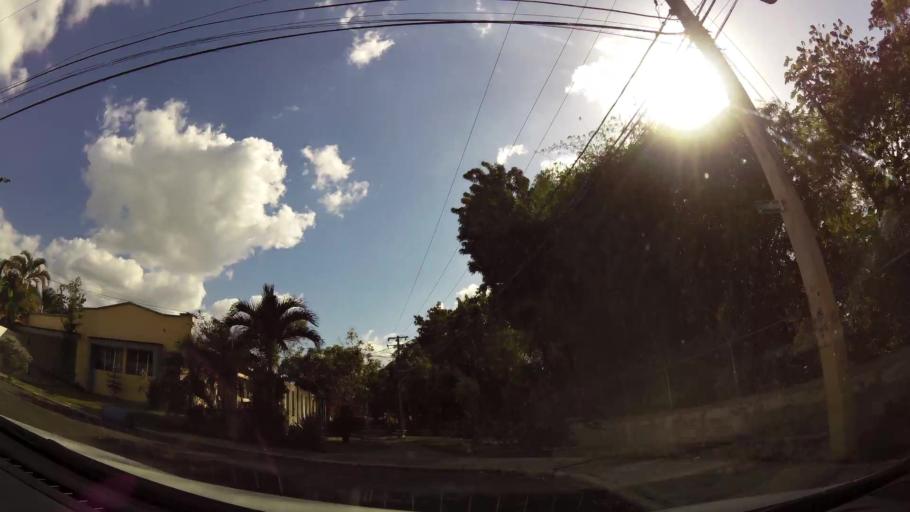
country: DO
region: Nacional
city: Santo Domingo
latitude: 18.5120
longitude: -69.9871
